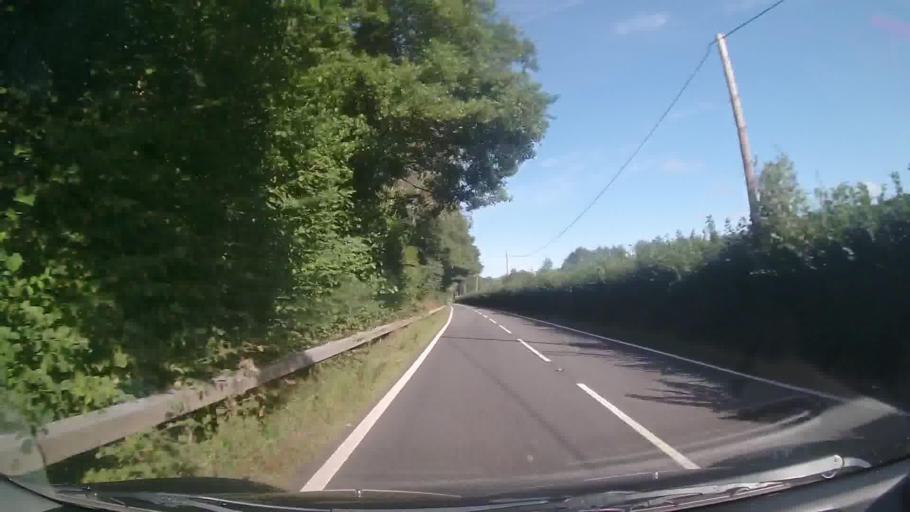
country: GB
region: Wales
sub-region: Blaenau Gwent
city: Brynmawr
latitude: 51.9231
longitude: -3.1870
